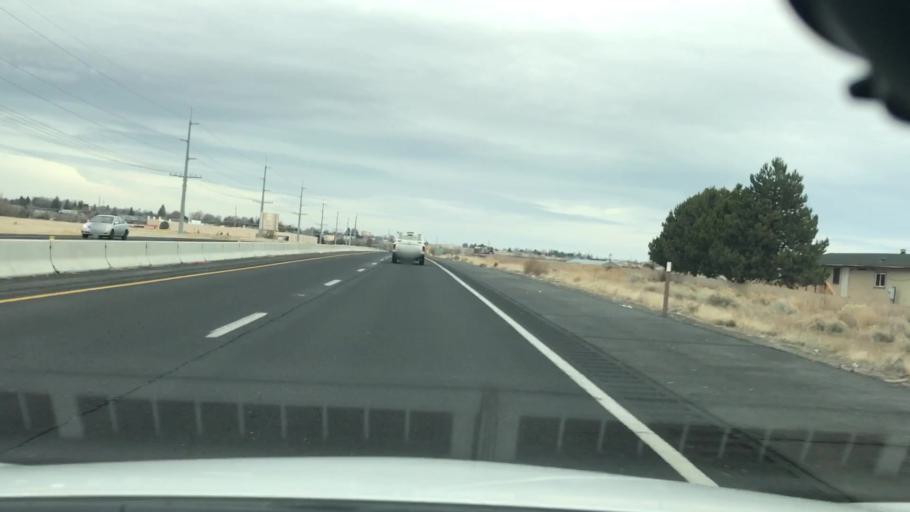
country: US
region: Washington
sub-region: Grant County
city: Moses Lake
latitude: 47.1466
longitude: -119.2864
